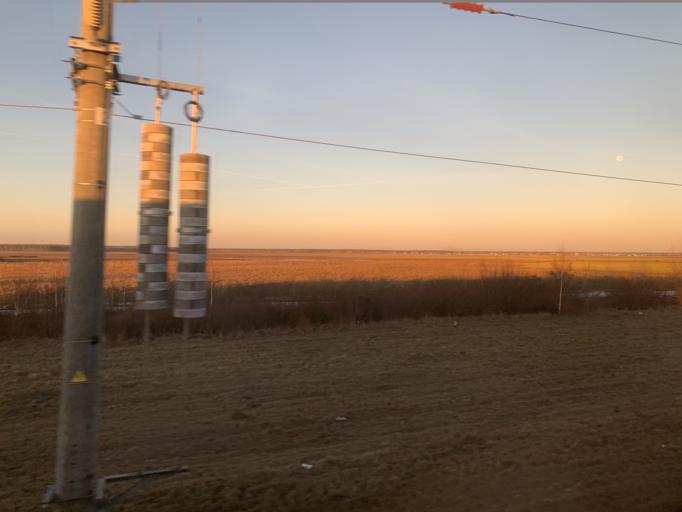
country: BY
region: Minsk
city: Nasilava
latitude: 54.3181
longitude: 26.7829
